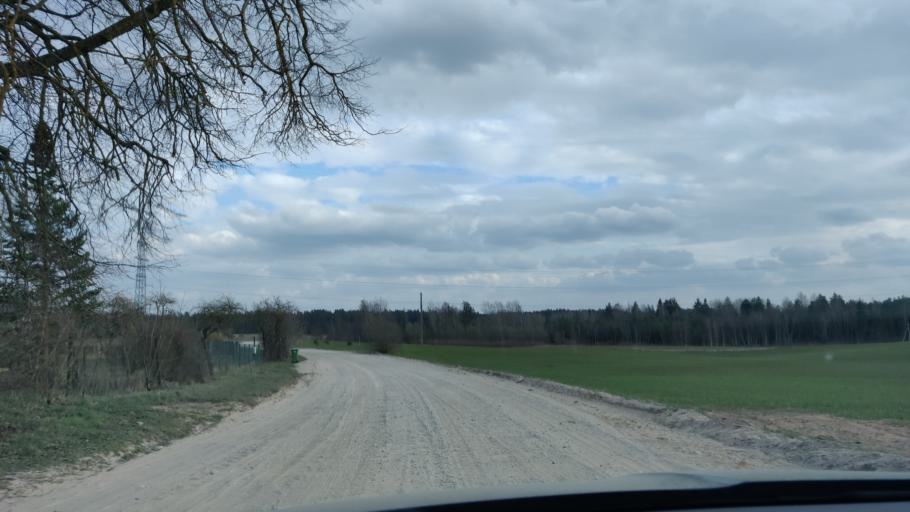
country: LT
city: Lentvaris
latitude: 54.6099
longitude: 25.0712
